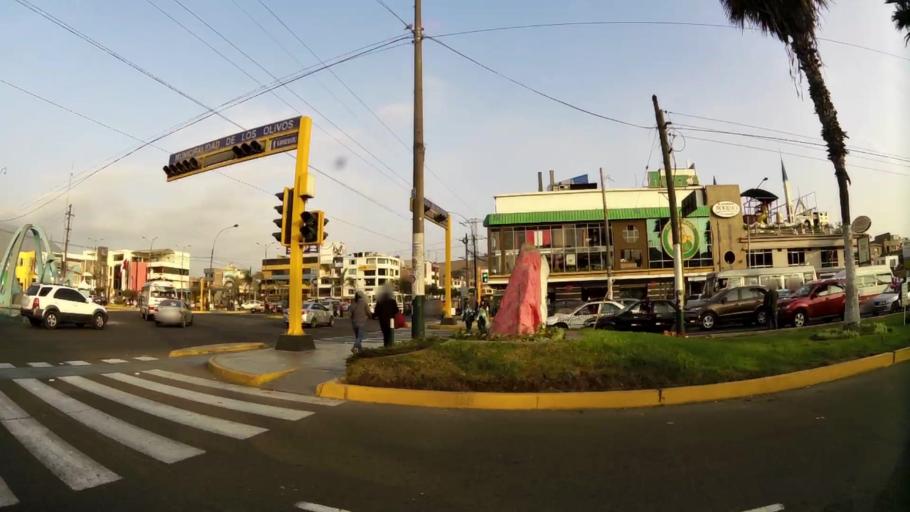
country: PE
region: Lima
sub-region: Lima
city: Independencia
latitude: -11.9913
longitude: -77.0720
